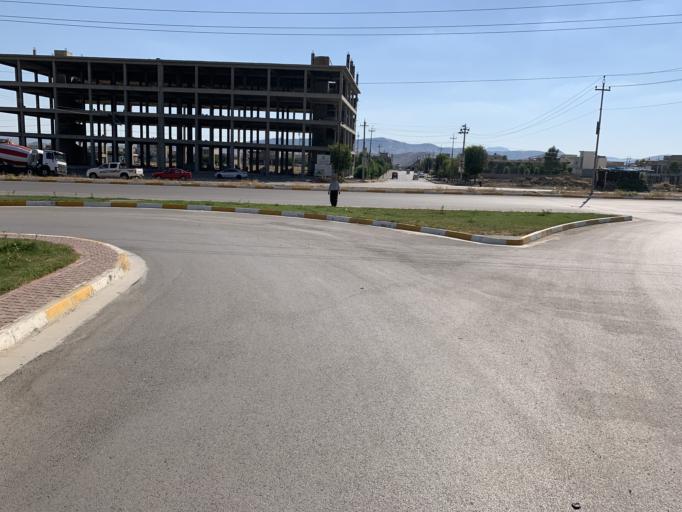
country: IQ
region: As Sulaymaniyah
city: Raniye
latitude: 36.2321
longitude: 44.7865
